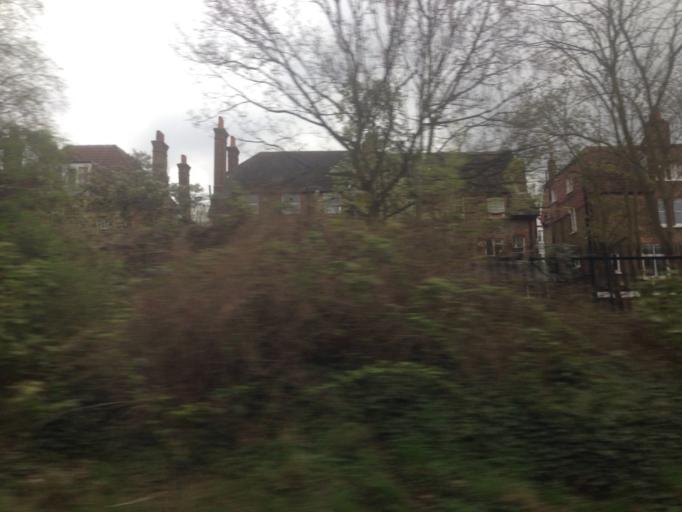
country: GB
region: England
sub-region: Greater London
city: Brixton Hill
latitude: 51.4296
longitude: -0.1384
